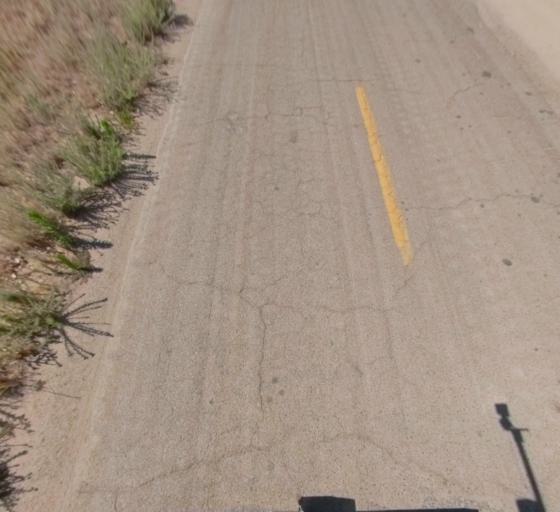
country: US
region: California
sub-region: Fresno County
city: Biola
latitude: 36.8593
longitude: -119.9294
